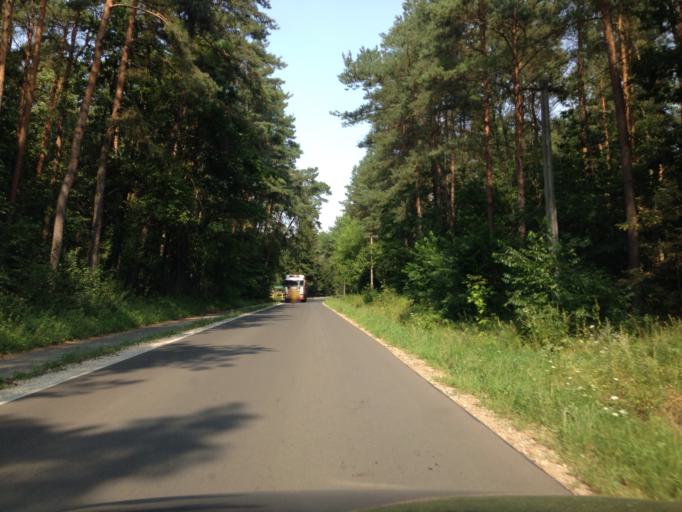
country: PL
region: Kujawsko-Pomorskie
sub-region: Powiat golubsko-dobrzynski
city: Golub-Dobrzyn
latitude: 53.0795
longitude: 19.0309
